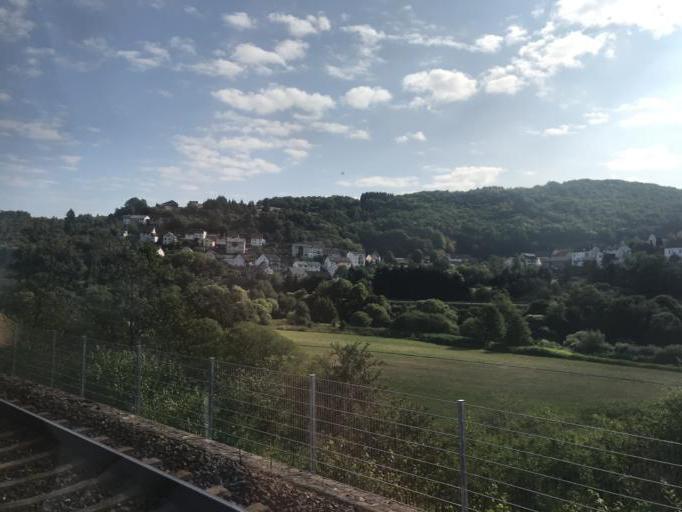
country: DE
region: Rheinland-Pfalz
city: Frauenberg
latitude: 49.6707
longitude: 7.2843
